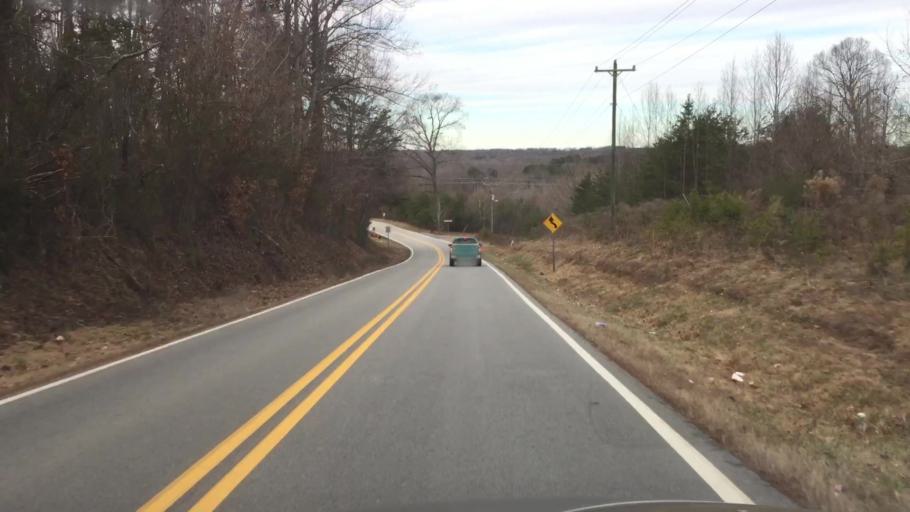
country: US
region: North Carolina
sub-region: Rockingham County
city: Reidsville
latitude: 36.3922
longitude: -79.6561
